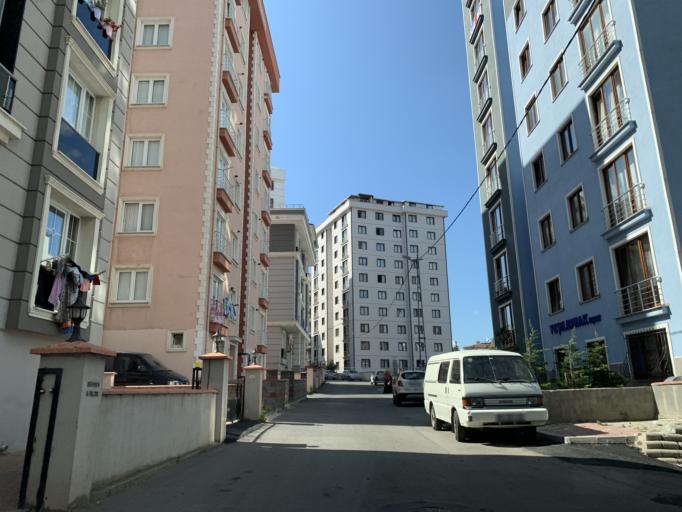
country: TR
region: Istanbul
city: Pendik
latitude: 40.8909
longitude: 29.2738
